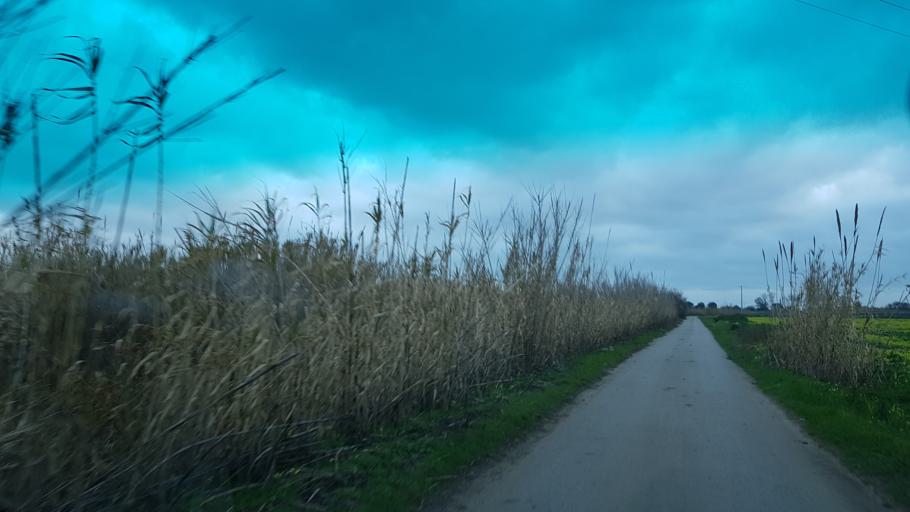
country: IT
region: Apulia
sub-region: Provincia di Brindisi
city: La Rosa
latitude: 40.5995
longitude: 17.9698
